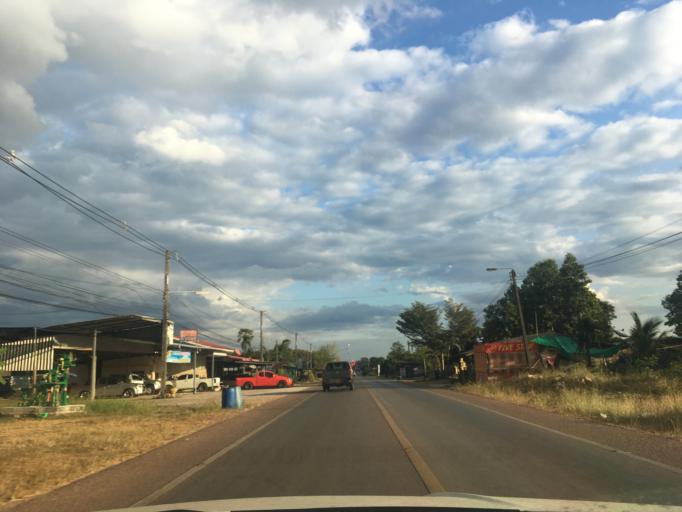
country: TH
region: Chanthaburi
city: Na Yai Am
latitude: 12.7342
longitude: 101.7452
